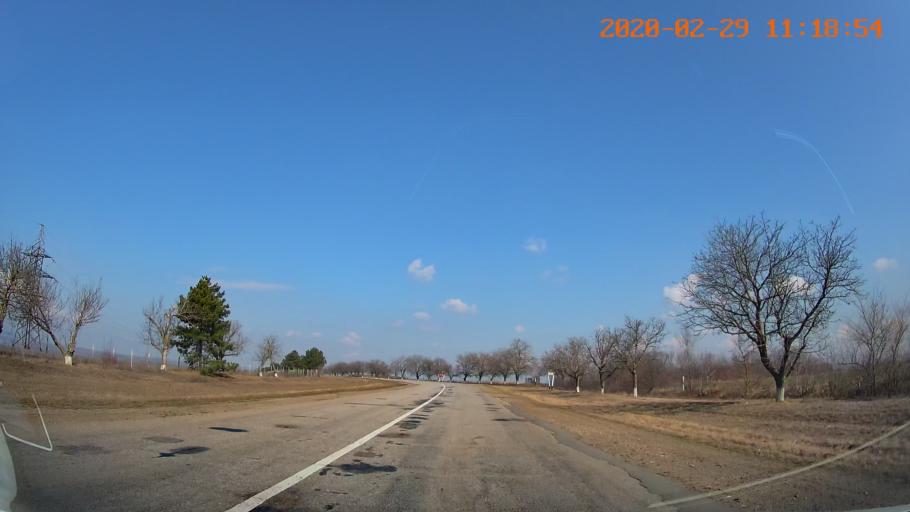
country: MD
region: Telenesti
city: Cocieri
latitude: 47.3418
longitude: 29.1758
